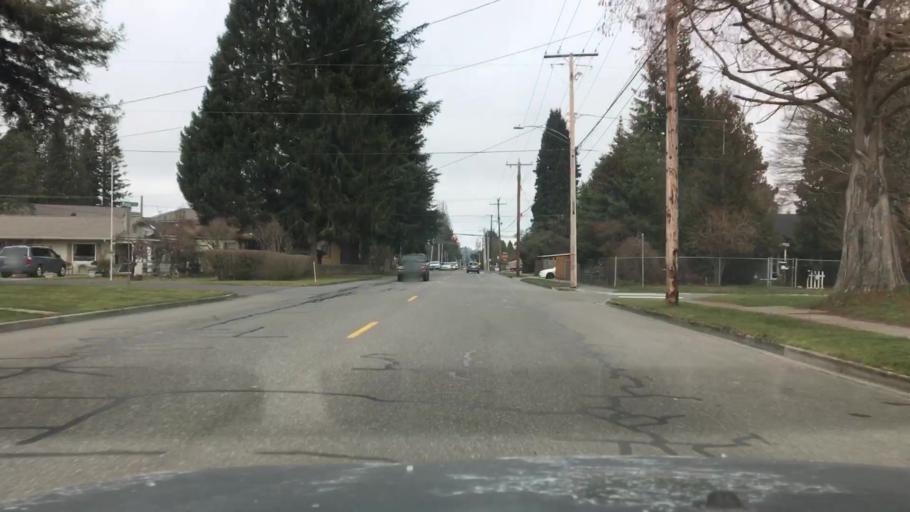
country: US
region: Washington
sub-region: Skagit County
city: Sedro-Woolley
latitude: 48.5021
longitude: -122.2259
